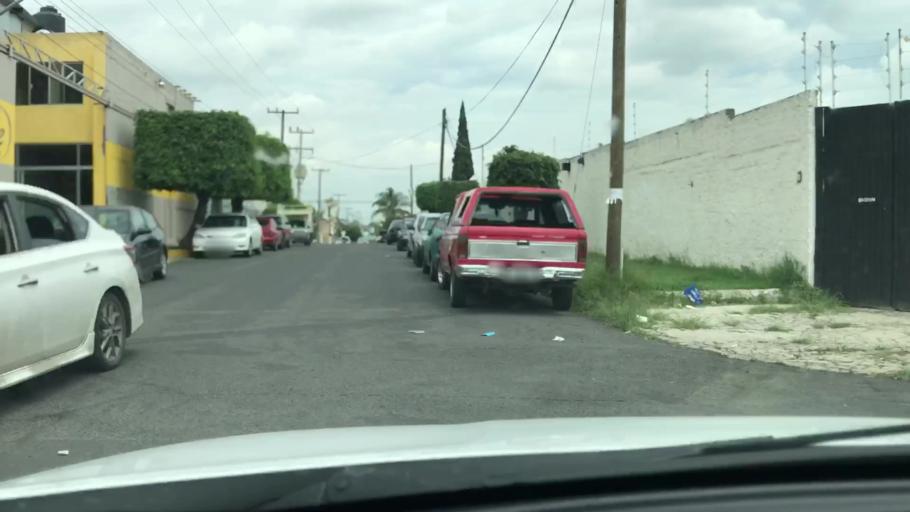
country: MX
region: Jalisco
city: Guadalajara
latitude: 20.6438
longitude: -103.4378
